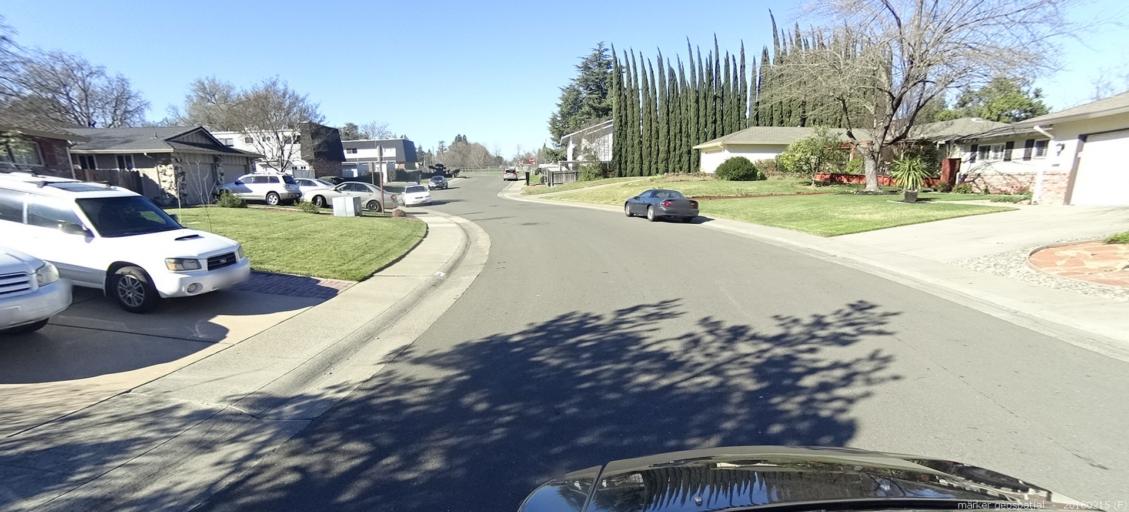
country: US
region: California
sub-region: Sacramento County
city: Foothill Farms
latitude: 38.6630
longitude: -121.3354
